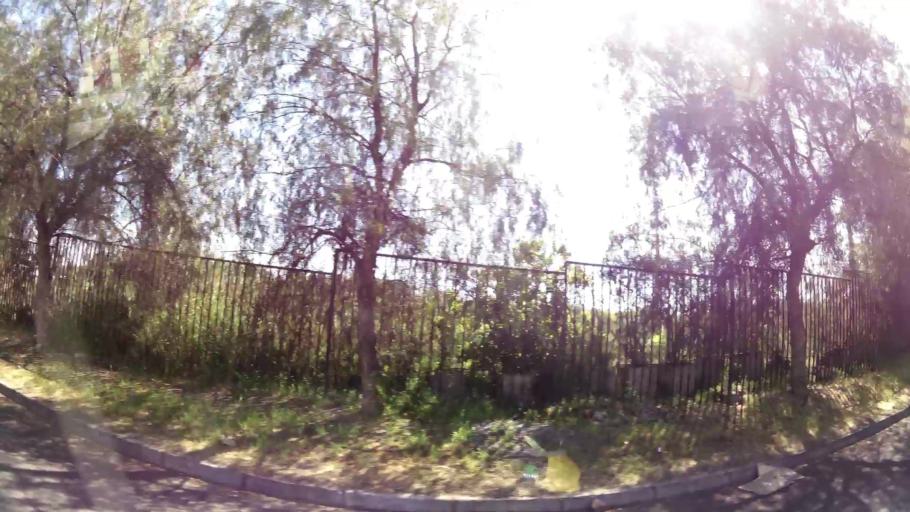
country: CL
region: Santiago Metropolitan
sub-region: Provincia de Santiago
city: Villa Presidente Frei, Nunoa, Santiago, Chile
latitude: -33.4326
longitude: -70.5318
